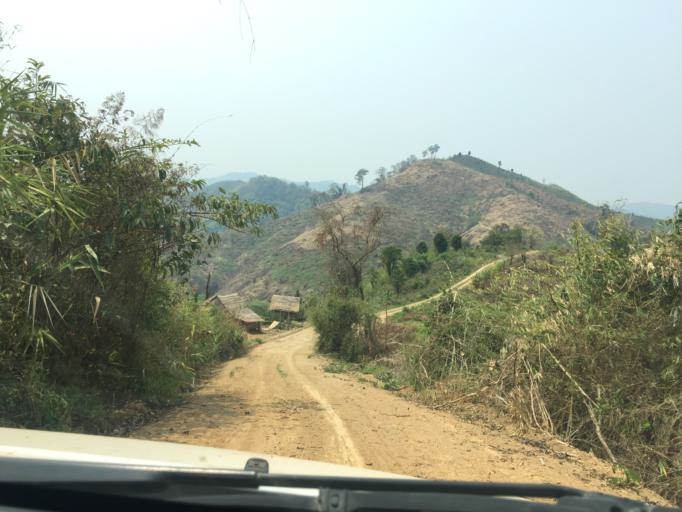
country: LA
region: Loungnamtha
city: Muang Nale
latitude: 20.6204
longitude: 101.6189
